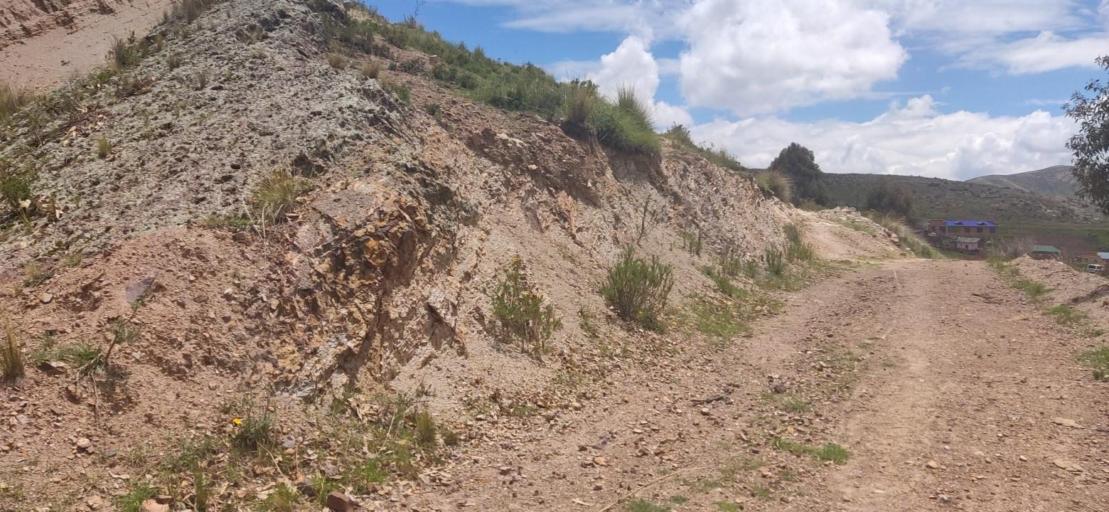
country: BO
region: La Paz
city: Batallas
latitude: -16.3443
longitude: -68.6382
